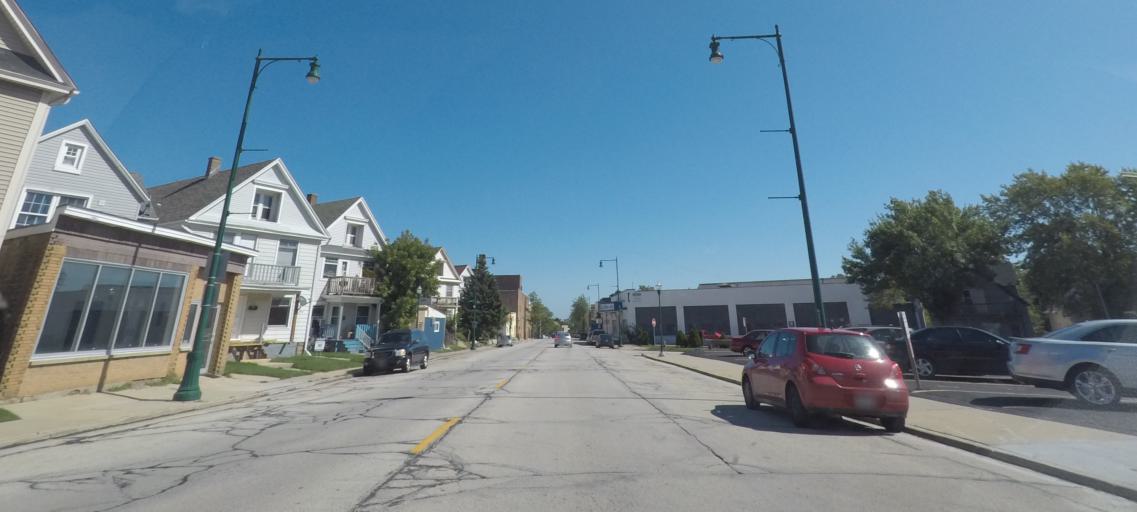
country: US
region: Wisconsin
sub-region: Milwaukee County
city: West Allis
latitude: 43.0155
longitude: -87.9929
